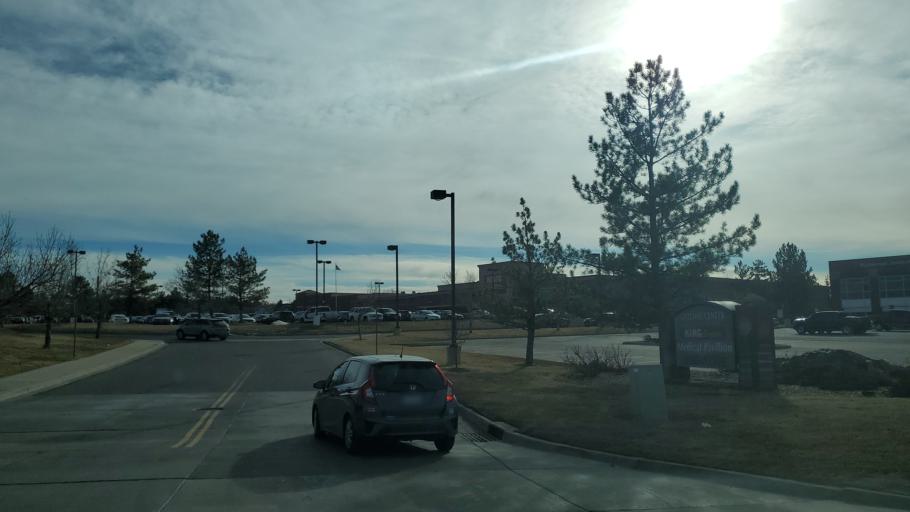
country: US
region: Colorado
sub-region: Douglas County
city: Acres Green
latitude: 39.5604
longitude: -104.9071
